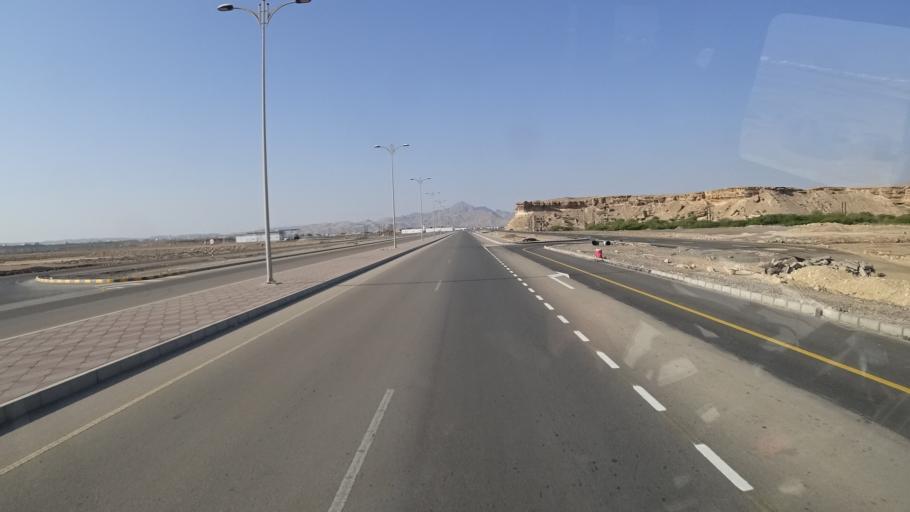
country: OM
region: Ash Sharqiyah
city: Sur
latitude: 22.5950
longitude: 59.4789
